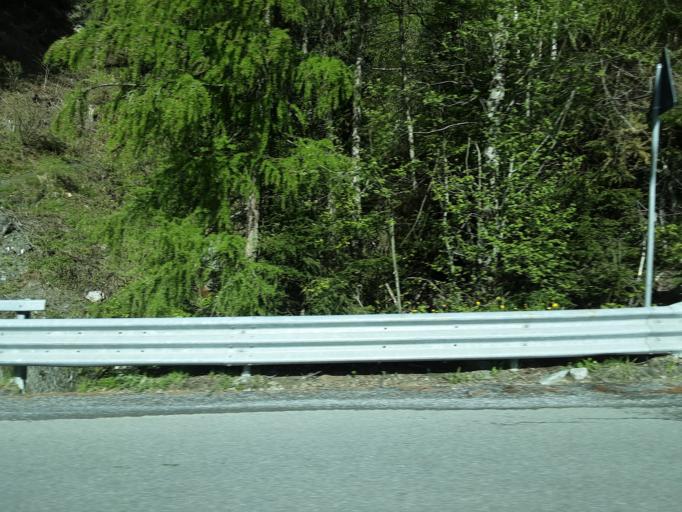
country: IT
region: Lombardy
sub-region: Provincia di Sondrio
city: Bormio
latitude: 46.4637
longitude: 10.3534
